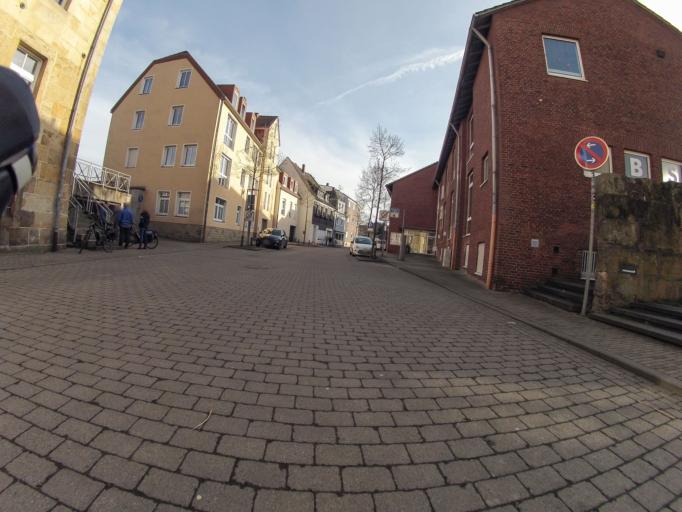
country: DE
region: North Rhine-Westphalia
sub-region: Regierungsbezirk Munster
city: Rheine
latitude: 52.2812
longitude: 7.4380
